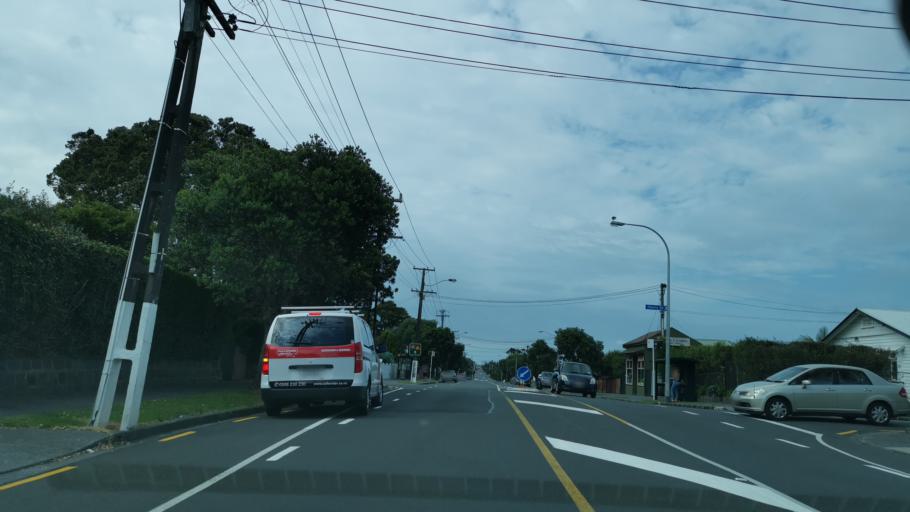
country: NZ
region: Auckland
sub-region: Auckland
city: Rosebank
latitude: -36.8907
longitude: 174.7007
